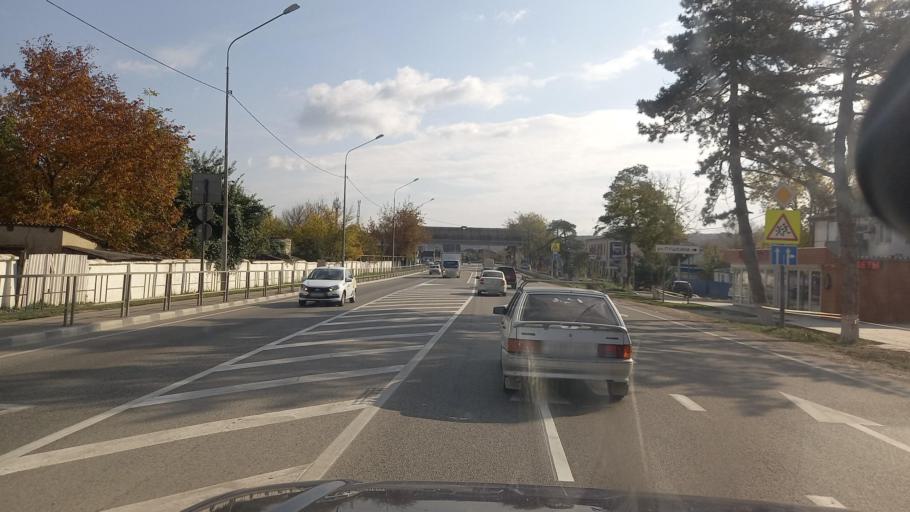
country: RU
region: Krasnodarskiy
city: Krymsk
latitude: 44.8683
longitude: 37.8634
